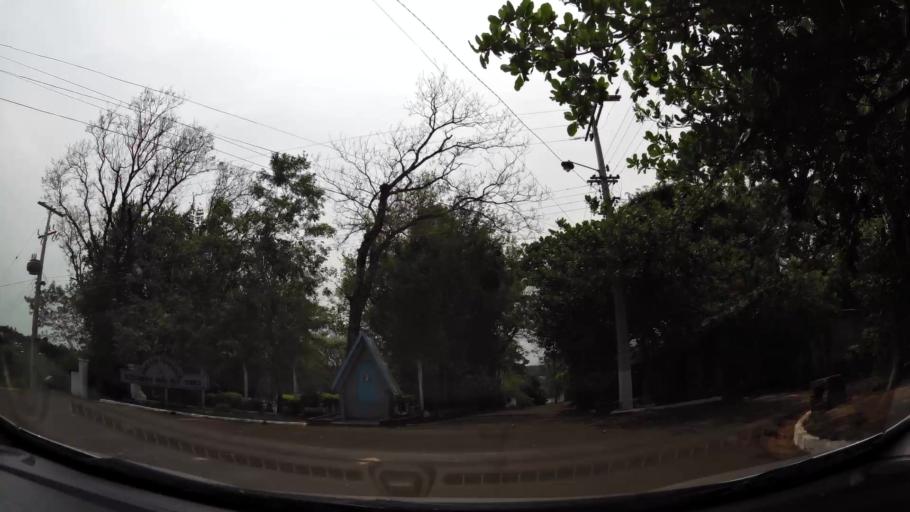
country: BR
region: Parana
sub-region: Foz Do Iguacu
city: Foz do Iguacu
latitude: -25.5568
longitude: -54.5989
